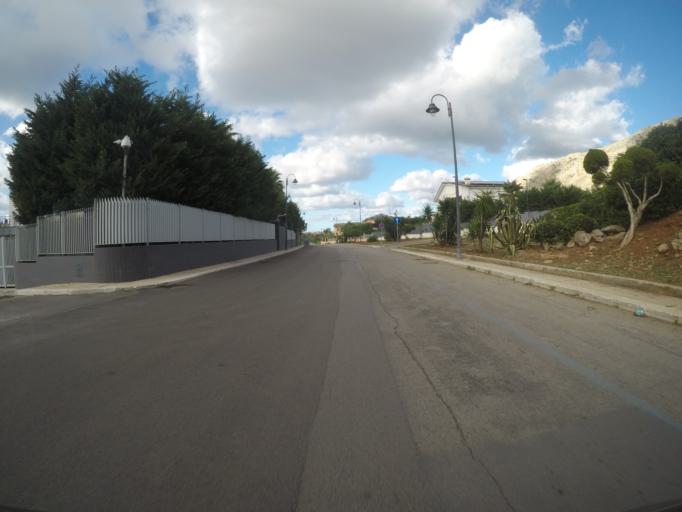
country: IT
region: Sicily
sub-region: Palermo
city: Isola delle Femmine
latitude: 38.1892
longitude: 13.2447
